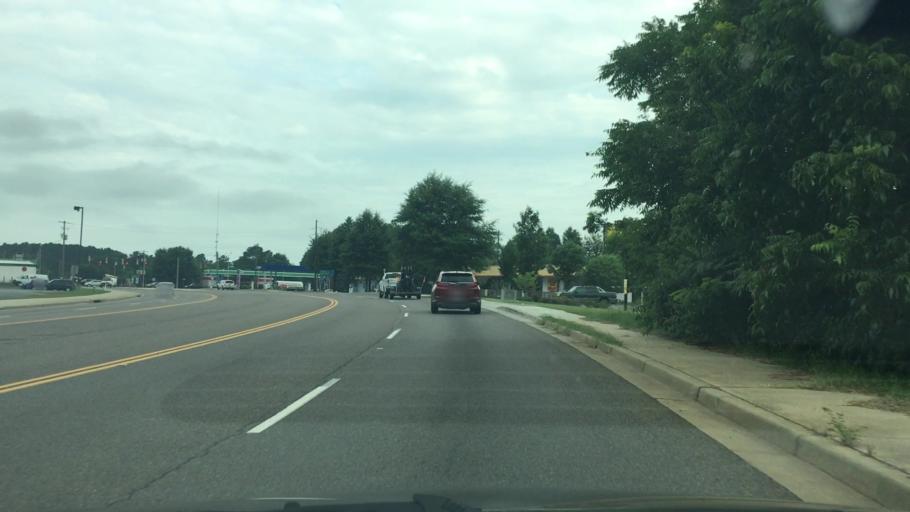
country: US
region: South Carolina
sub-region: Aiken County
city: Aiken
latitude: 33.5754
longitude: -81.7015
